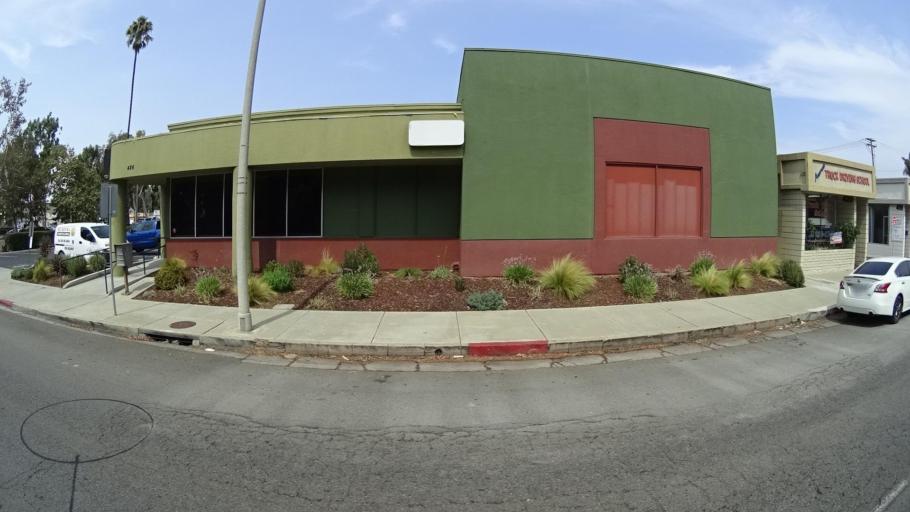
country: US
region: California
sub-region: San Diego County
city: Escondido
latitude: 33.1183
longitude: -117.0857
